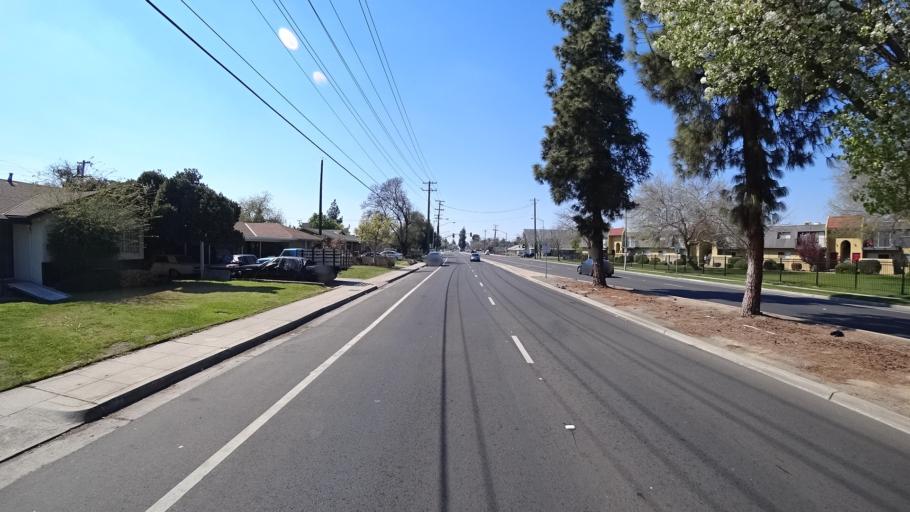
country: US
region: California
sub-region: Fresno County
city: Fresno
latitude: 36.7937
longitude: -119.8339
